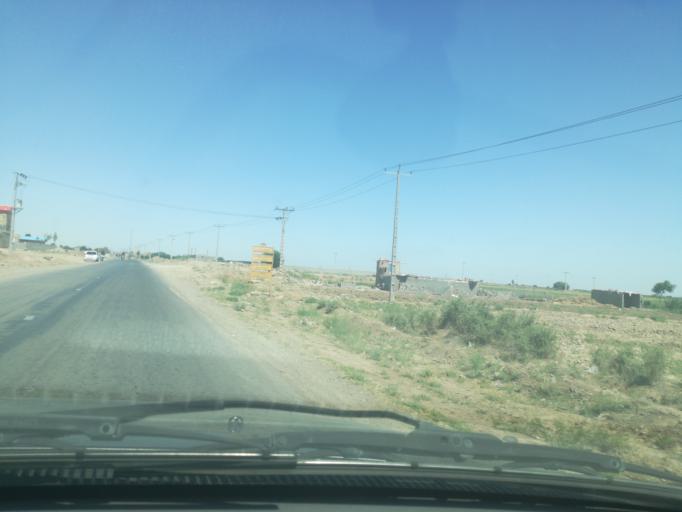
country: IR
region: Razavi Khorasan
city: Sarakhs
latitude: 36.5659
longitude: 61.1422
